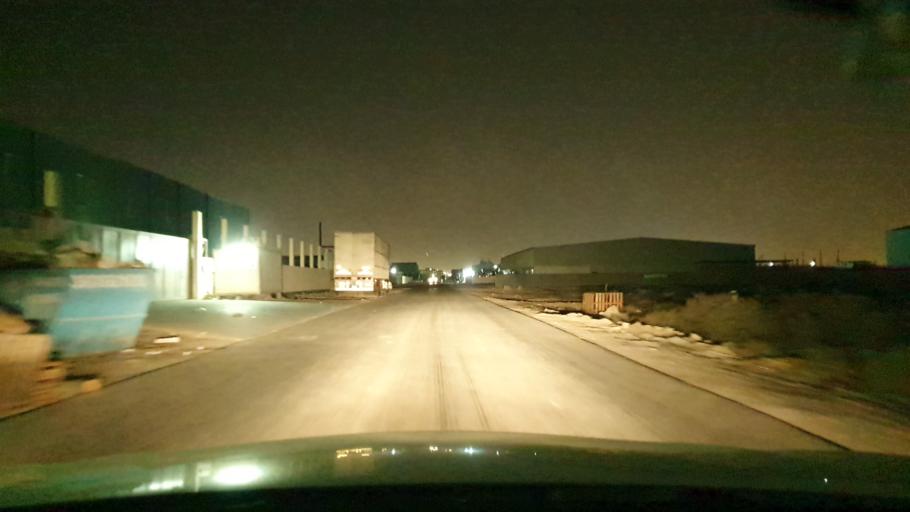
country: BH
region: Northern
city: Sitrah
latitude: 26.0973
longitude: 50.6252
